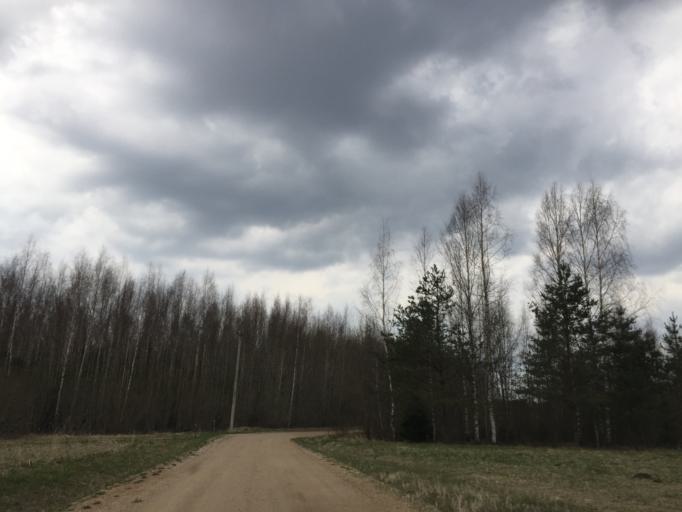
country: EE
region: Vorumaa
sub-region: Antsla vald
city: Vana-Antsla
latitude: 57.9439
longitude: 26.7188
